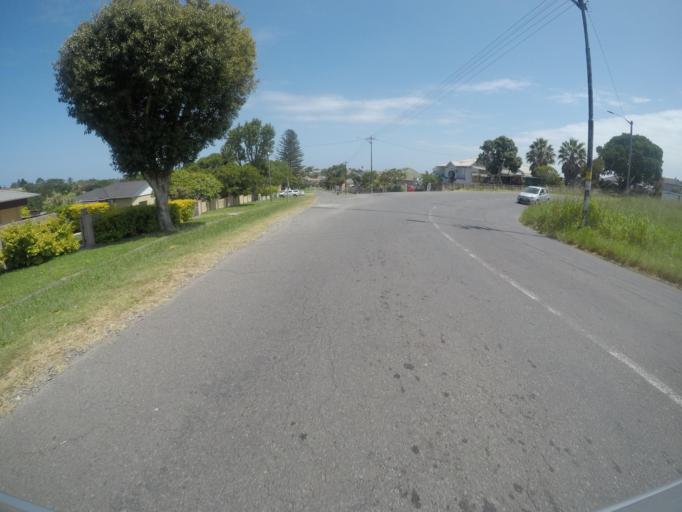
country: ZA
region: Eastern Cape
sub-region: Buffalo City Metropolitan Municipality
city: East London
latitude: -32.9735
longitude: 27.8764
